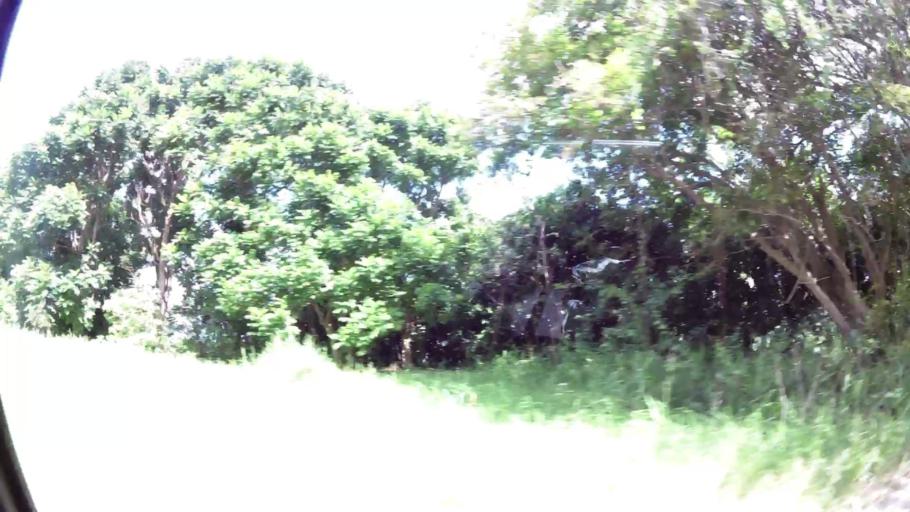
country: BB
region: Saint James
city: Holetown
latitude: 13.2150
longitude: -59.6073
